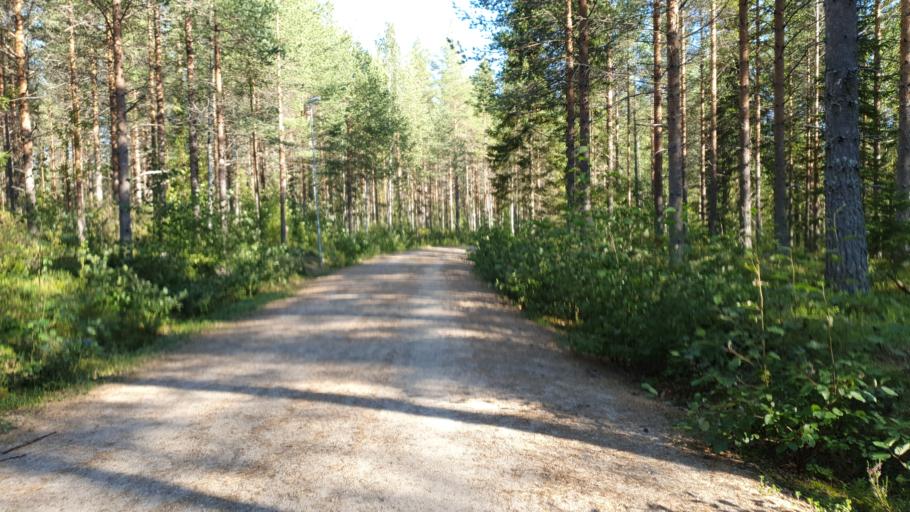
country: FI
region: Kainuu
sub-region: Kehys-Kainuu
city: Kuhmo
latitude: 64.1126
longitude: 29.5044
